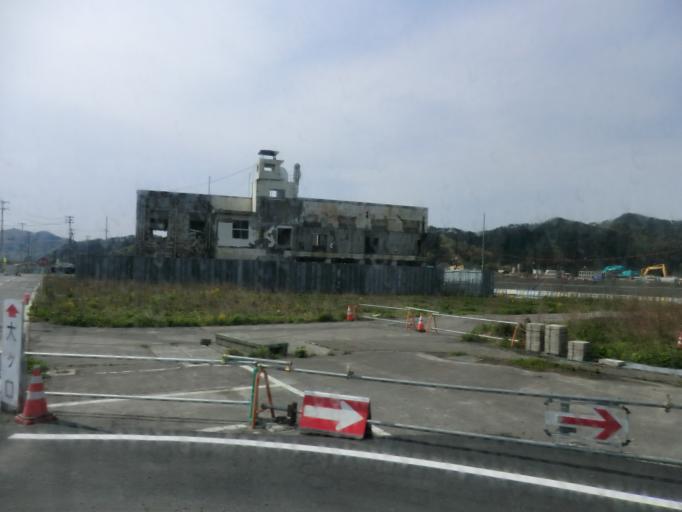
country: JP
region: Iwate
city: Otsuchi
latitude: 39.3604
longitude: 141.9067
